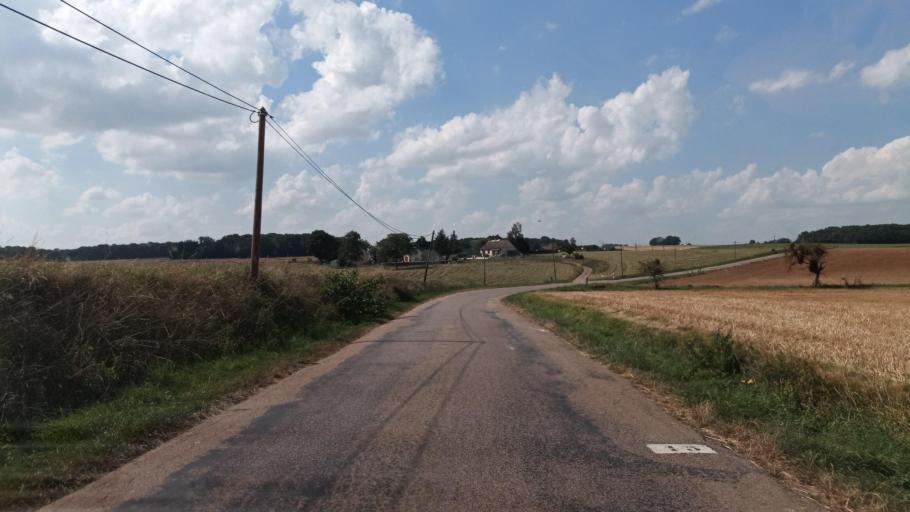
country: FR
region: Bourgogne
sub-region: Departement de l'Yonne
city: Egriselles-le-Bocage
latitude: 48.0256
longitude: 3.1715
